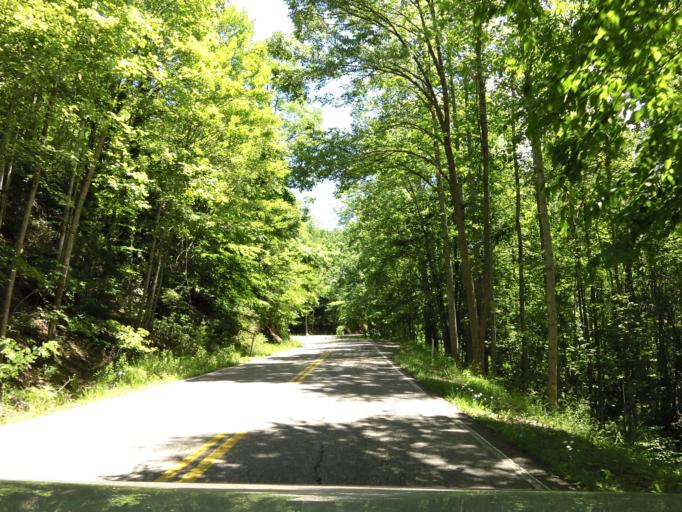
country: US
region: North Carolina
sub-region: Graham County
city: Robbinsville
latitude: 35.4771
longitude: -83.9219
